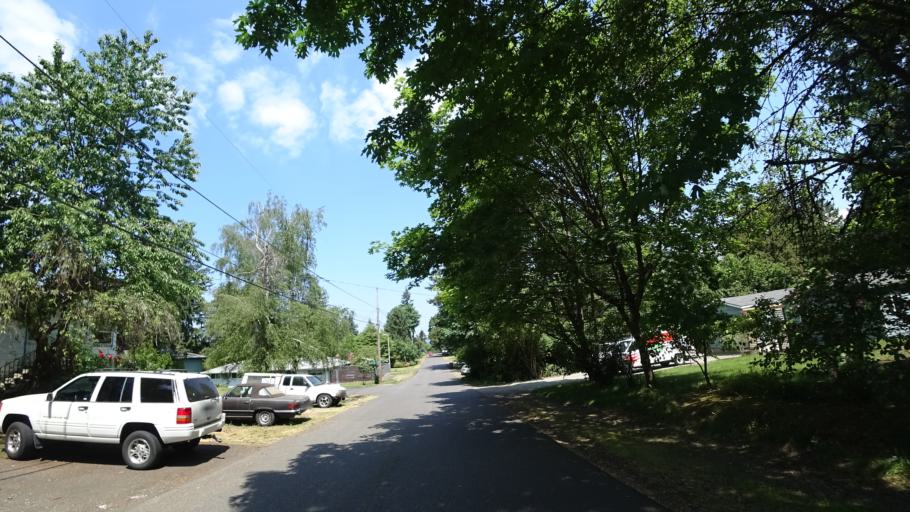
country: US
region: Oregon
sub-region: Multnomah County
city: Fairview
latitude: 45.5298
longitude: -122.5038
